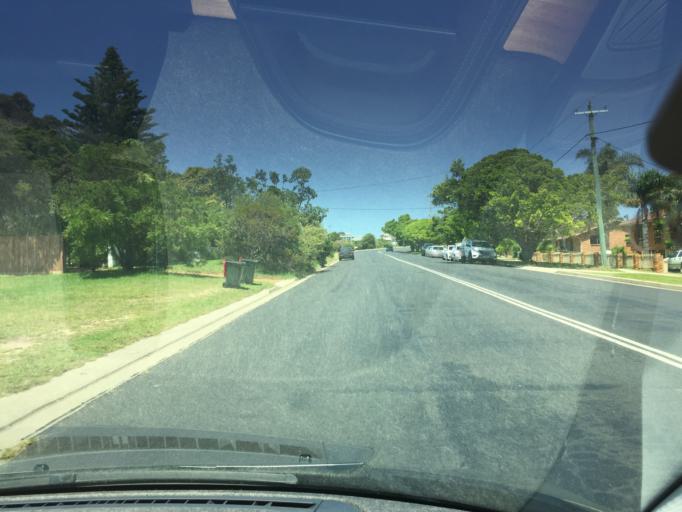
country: AU
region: New South Wales
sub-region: Bega Valley
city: Bega
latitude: -36.7305
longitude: 149.9850
